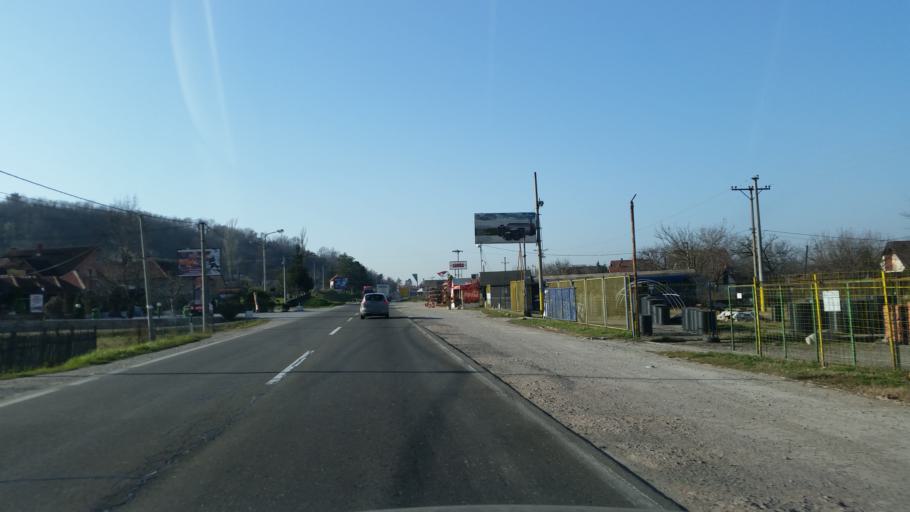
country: RS
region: Central Serbia
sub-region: Kolubarski Okrug
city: Lajkovac
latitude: 44.3673
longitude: 20.2032
